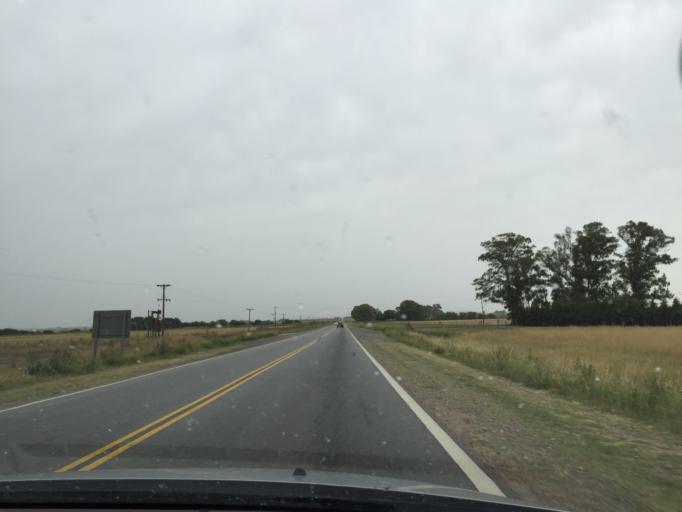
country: AR
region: Buenos Aires
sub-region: Partido de Tandil
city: Tandil
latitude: -37.5623
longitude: -58.7877
